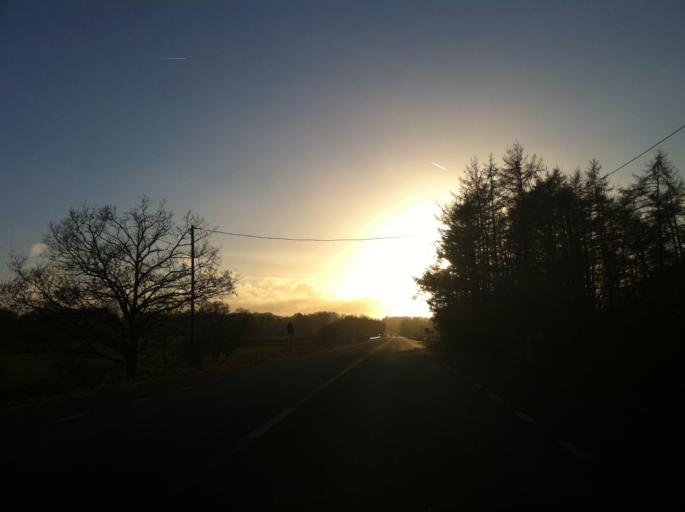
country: SE
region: Skane
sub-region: Hassleholms Kommun
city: Tormestorp
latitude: 56.1070
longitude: 13.7823
